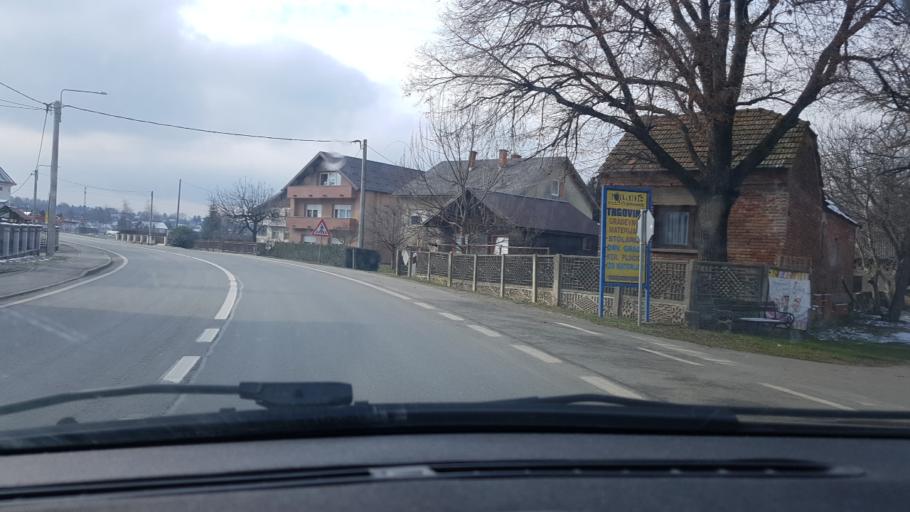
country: HR
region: Varazdinska
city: Tuzno
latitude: 46.2830
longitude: 16.2130
